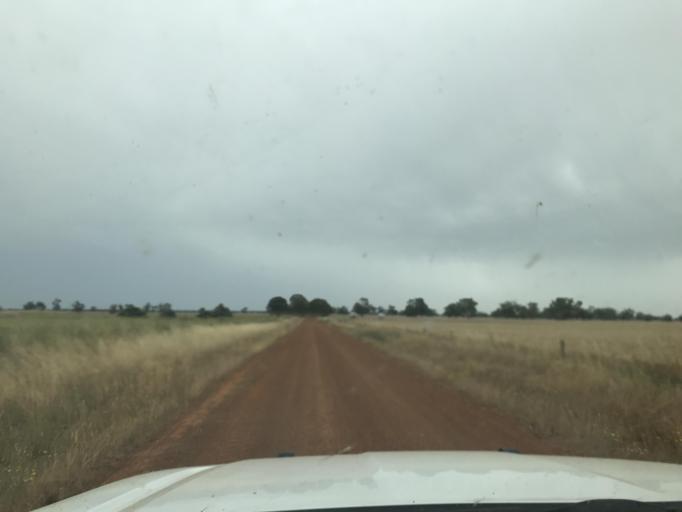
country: AU
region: Victoria
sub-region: Horsham
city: Horsham
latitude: -37.0631
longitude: 141.6355
